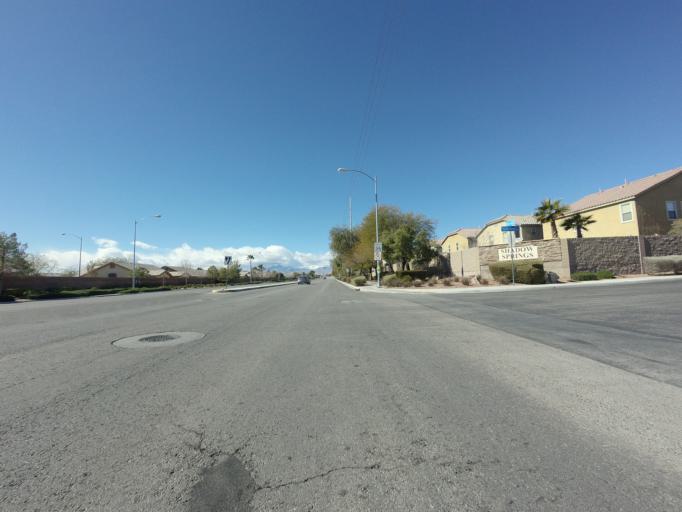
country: US
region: Nevada
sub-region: Clark County
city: Nellis Air Force Base
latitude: 36.2692
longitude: -115.1010
